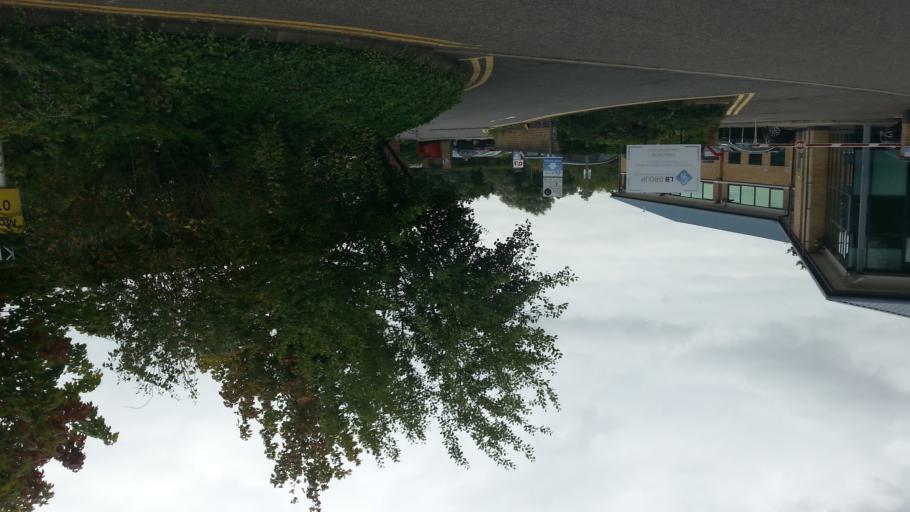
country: GB
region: England
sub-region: Essex
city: Chelmsford
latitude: 51.7408
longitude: 0.4786
